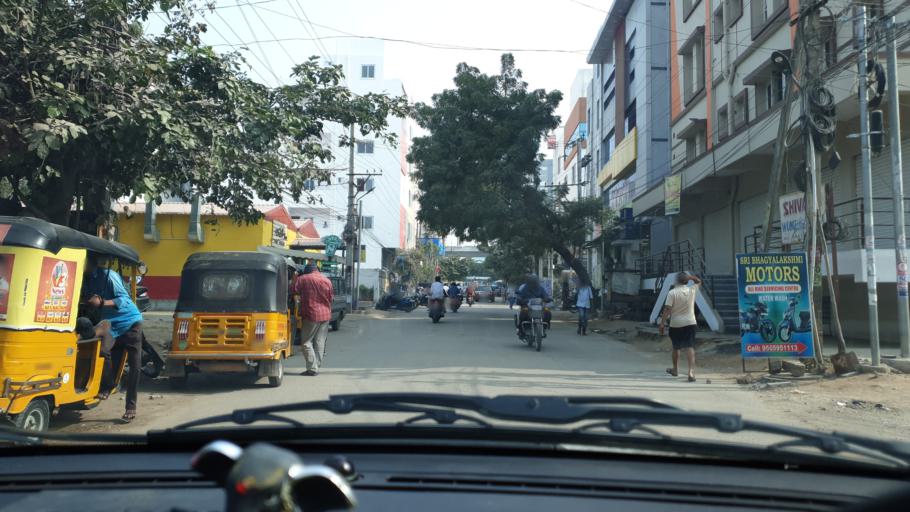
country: IN
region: Telangana
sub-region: Rangareddi
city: Kukatpalli
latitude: 17.4843
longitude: 78.4091
